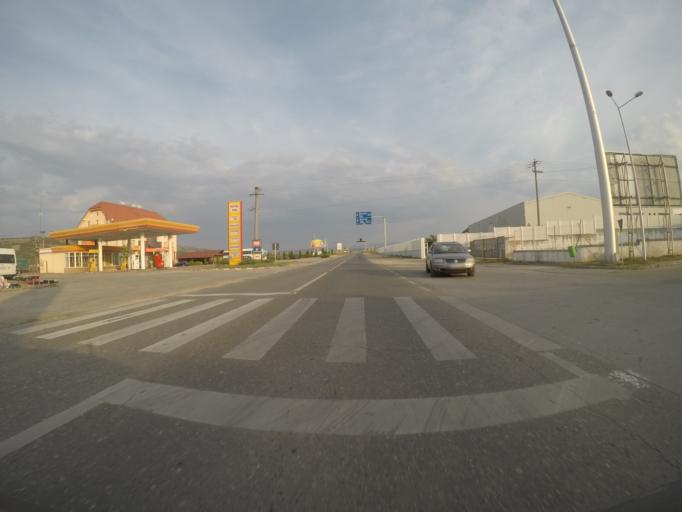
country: RO
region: Alba
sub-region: Municipiul Sebes
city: Sebes
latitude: 45.9477
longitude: 23.5862
